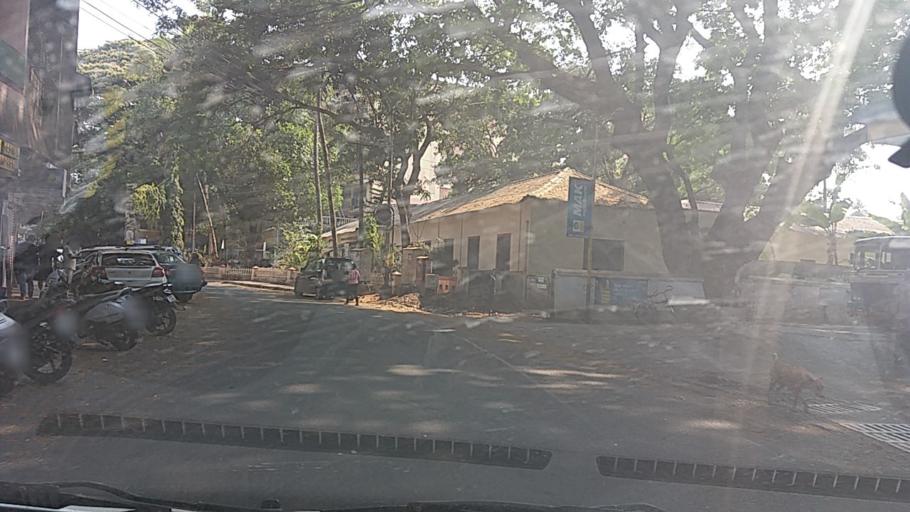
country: IN
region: Goa
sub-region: North Goa
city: Panaji
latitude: 15.4958
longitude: 73.8212
